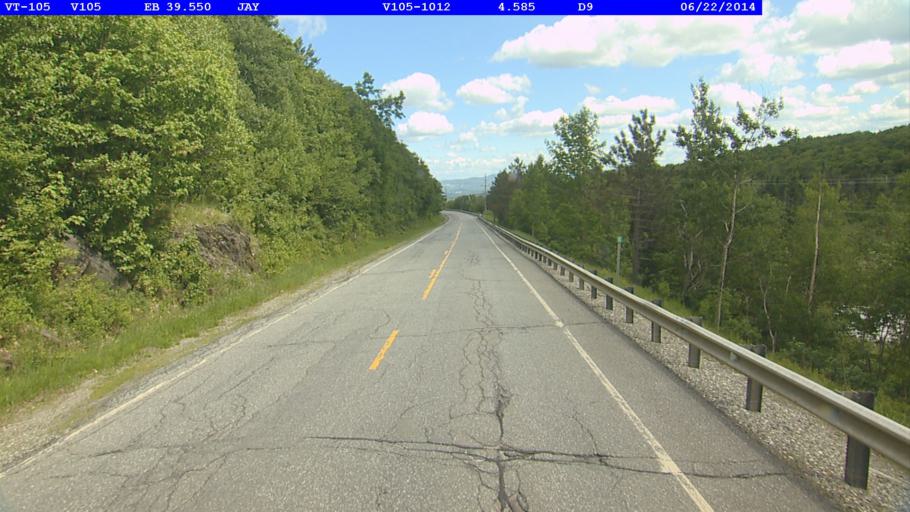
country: CA
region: Quebec
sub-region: Monteregie
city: Sutton
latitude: 44.9837
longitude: -72.4920
